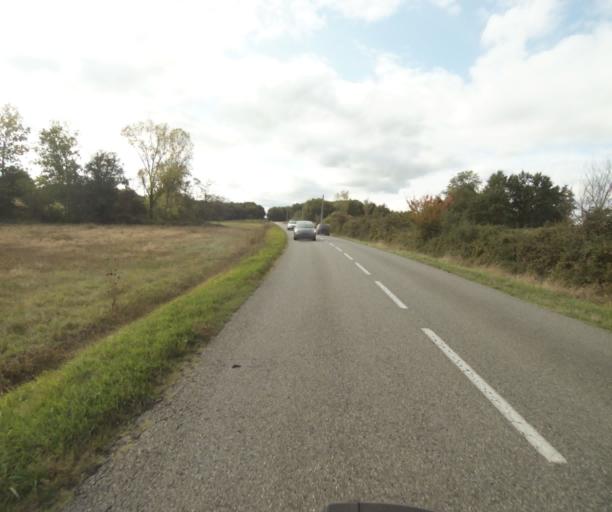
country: FR
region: Midi-Pyrenees
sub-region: Departement du Tarn-et-Garonne
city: Verdun-sur-Garonne
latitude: 43.8457
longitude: 1.1548
